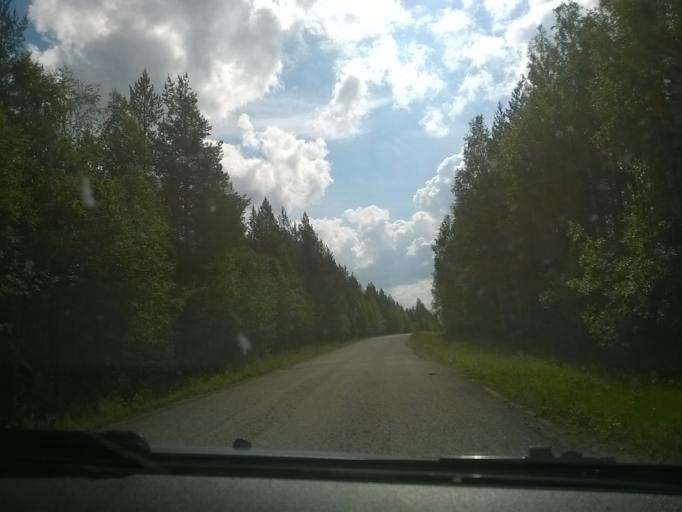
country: FI
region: Kainuu
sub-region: Kehys-Kainuu
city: Kuhmo
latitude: 64.4175
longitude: 29.7638
